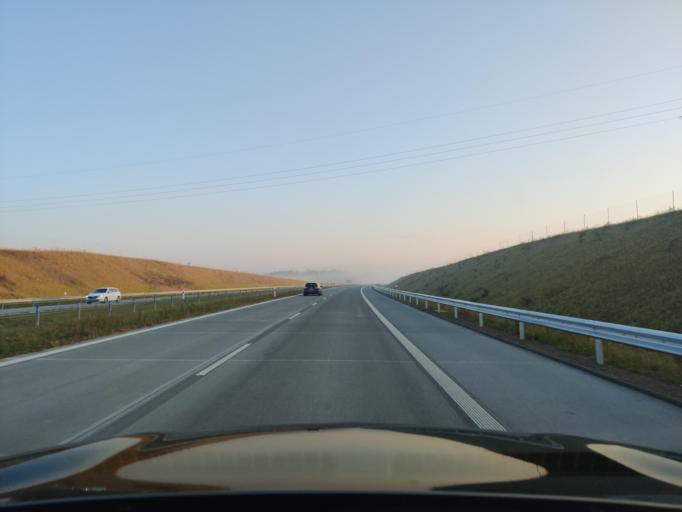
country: PL
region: Masovian Voivodeship
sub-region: Powiat mlawski
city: Mlawa
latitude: 53.1234
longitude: 20.4114
